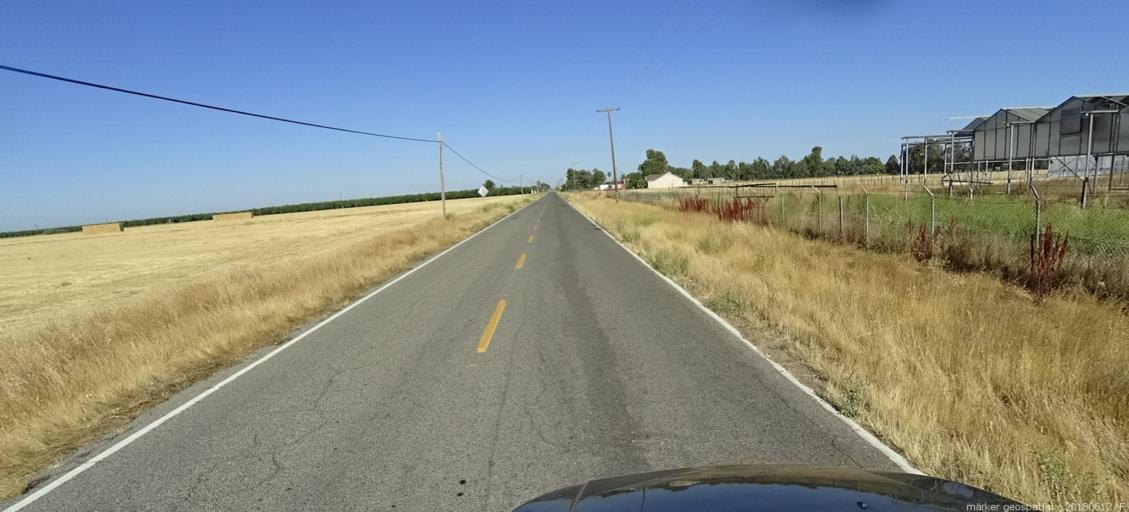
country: US
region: California
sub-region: Madera County
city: Madera Acres
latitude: 37.0110
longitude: -120.1230
